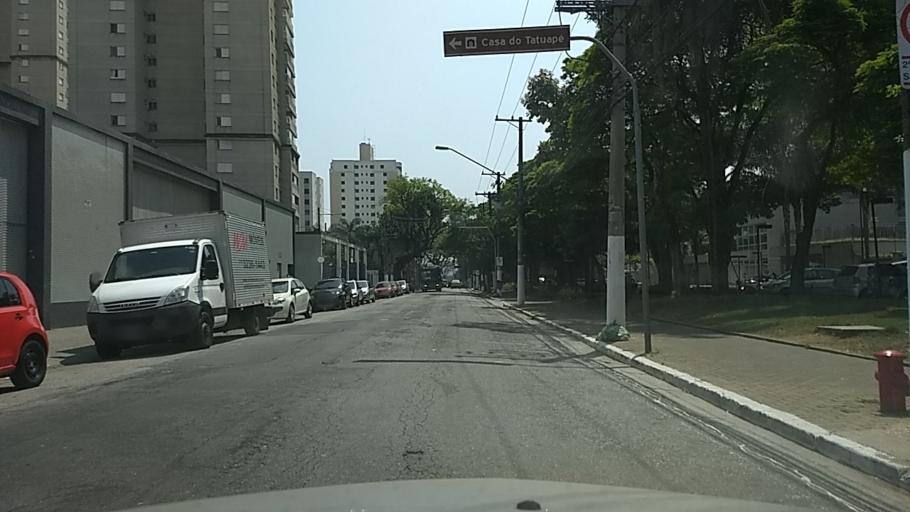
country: BR
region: Sao Paulo
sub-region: Sao Paulo
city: Sao Paulo
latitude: -23.5313
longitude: -46.5757
